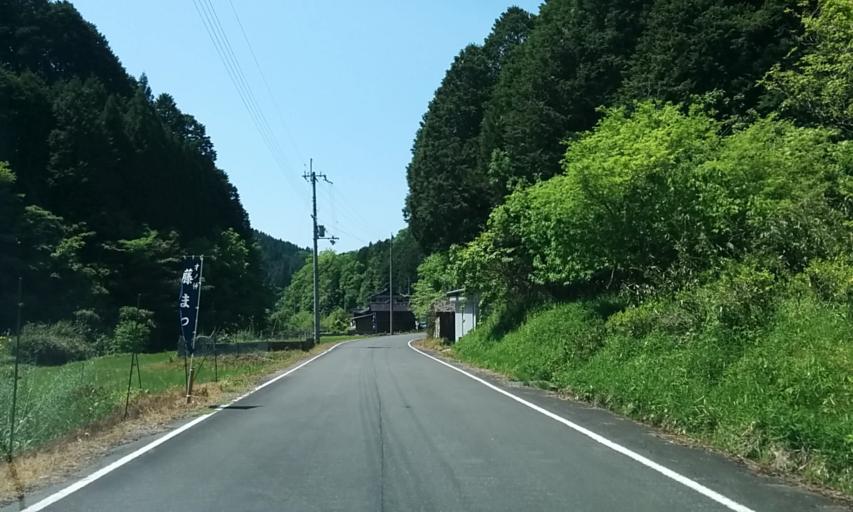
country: JP
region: Kyoto
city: Ayabe
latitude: 35.3812
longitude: 135.1913
